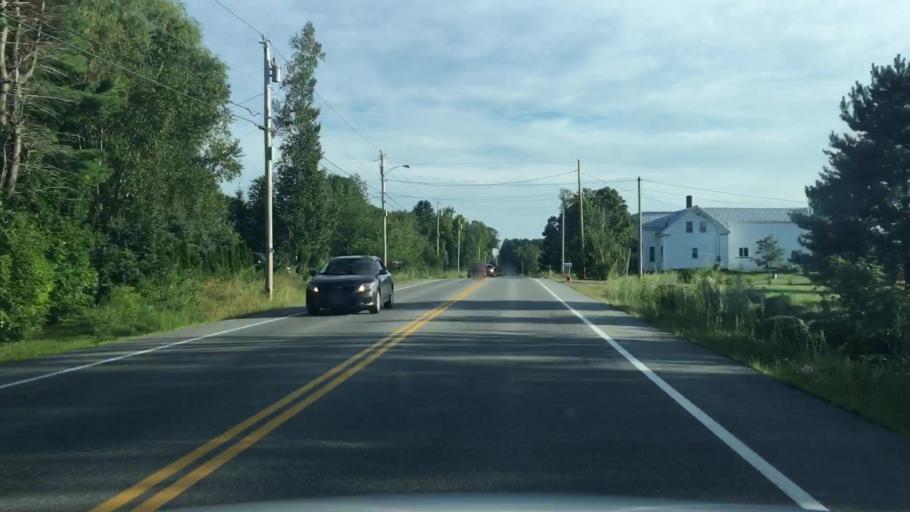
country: US
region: Maine
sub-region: Cumberland County
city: South Windham
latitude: 43.7809
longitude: -70.4397
